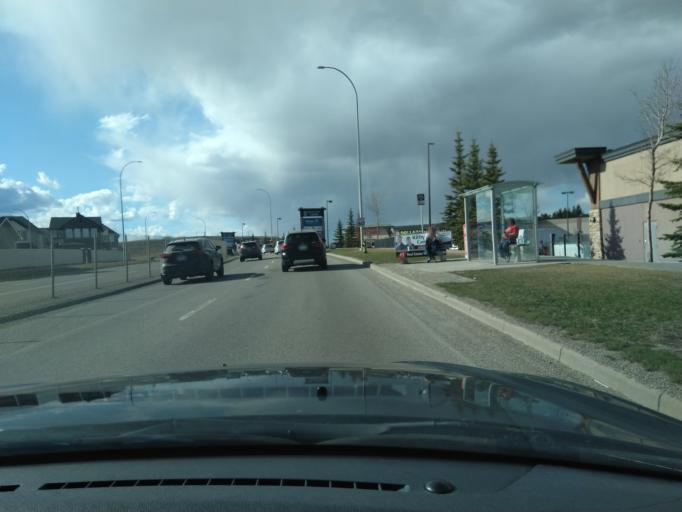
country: CA
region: Alberta
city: Calgary
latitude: 51.1524
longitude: -114.2159
